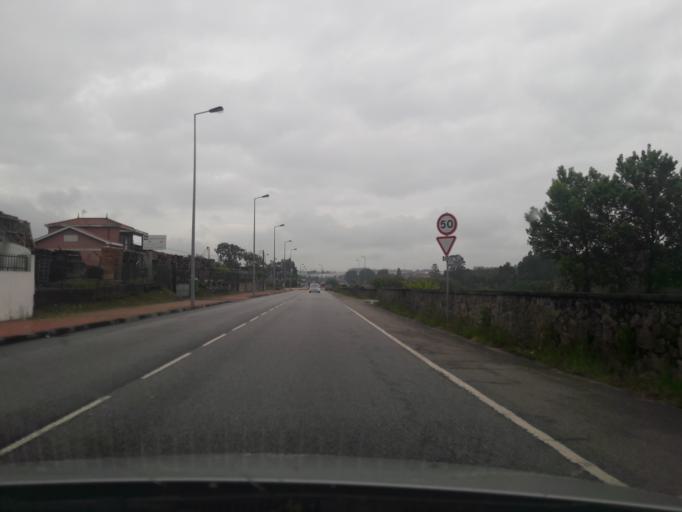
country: PT
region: Porto
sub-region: Vila do Conde
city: Arvore
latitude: 41.3401
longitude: -8.7313
